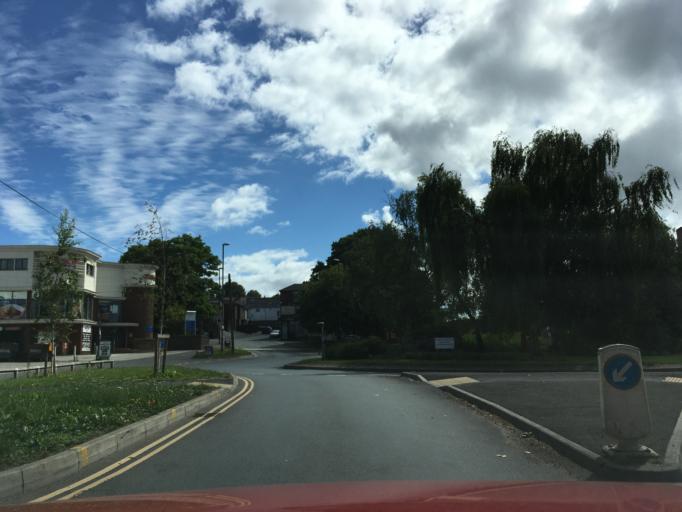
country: GB
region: England
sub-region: Nottingham
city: Nottingham
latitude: 52.9470
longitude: -1.1723
